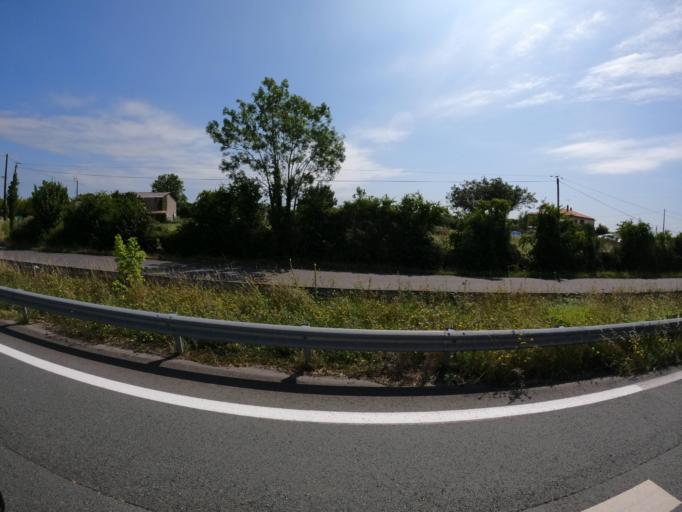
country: FR
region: Poitou-Charentes
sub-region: Departement des Deux-Sevres
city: Mauze-sur-le-Mignon
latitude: 46.1969
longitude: -0.6601
